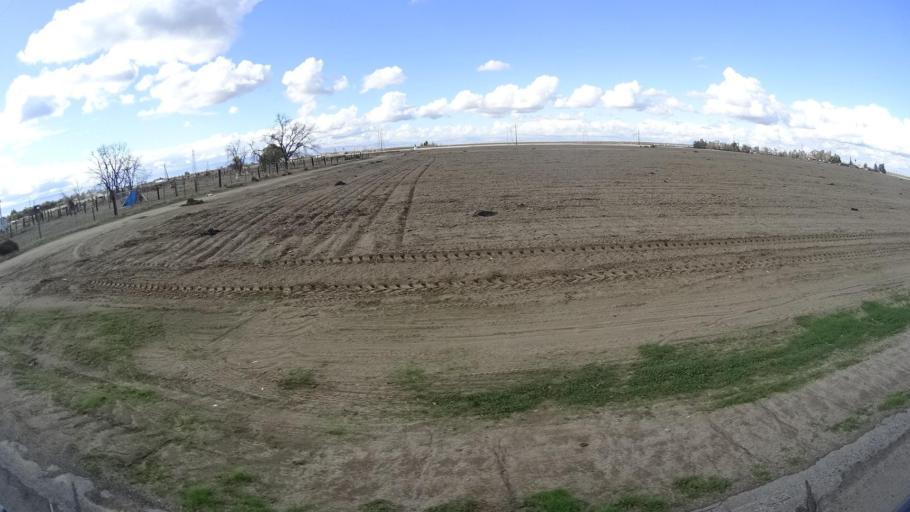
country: US
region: California
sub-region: Kern County
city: Greenfield
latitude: 35.2314
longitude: -119.0929
